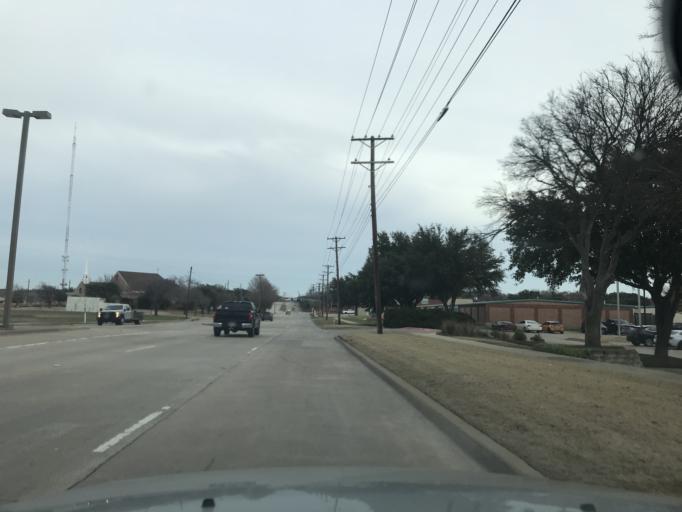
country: US
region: Texas
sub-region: Dallas County
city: Carrollton
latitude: 32.9972
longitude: -96.9229
